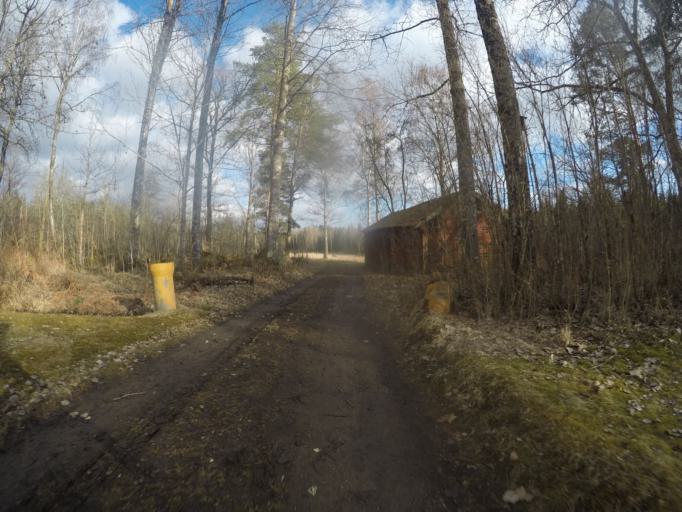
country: SE
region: Soedermanland
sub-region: Eskilstuna Kommun
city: Hallbybrunn
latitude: 59.3850
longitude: 16.4000
